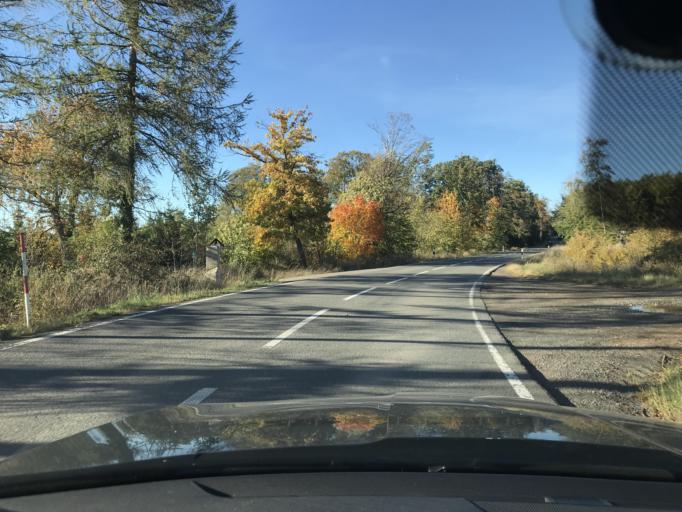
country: DE
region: Saxony-Anhalt
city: Friedrichsbrunn
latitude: 51.7086
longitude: 11.0160
